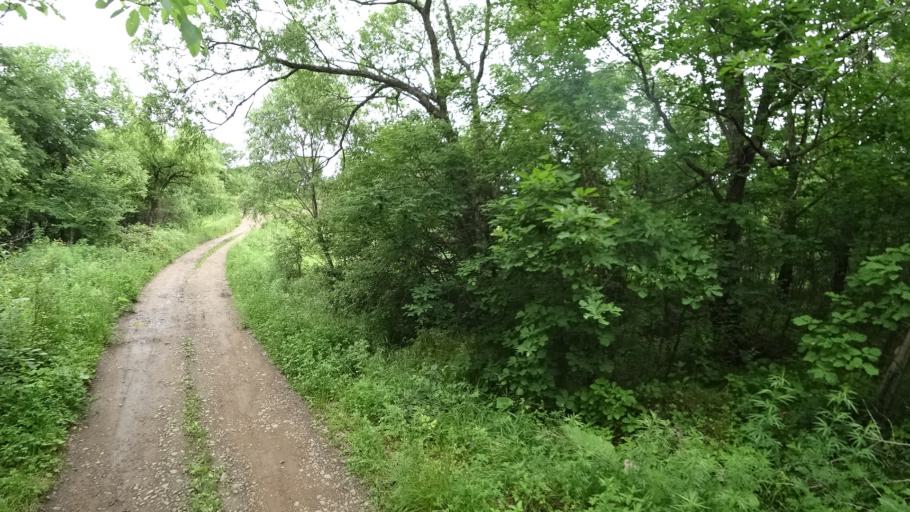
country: RU
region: Primorskiy
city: Novosysoyevka
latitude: 44.2094
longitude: 133.3282
